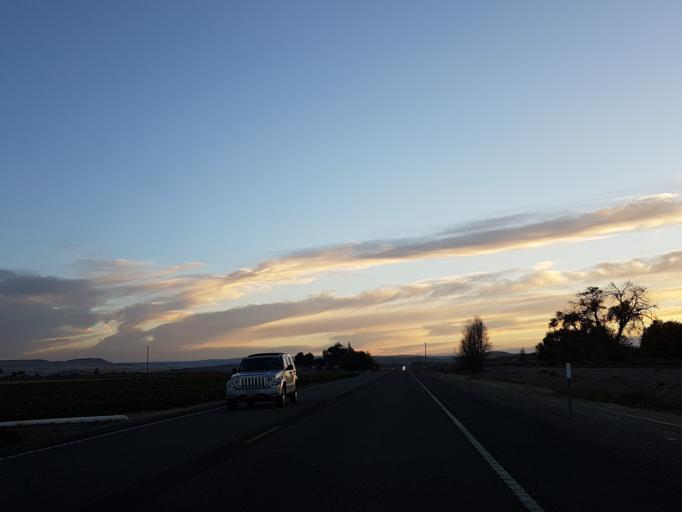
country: US
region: Oregon
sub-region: Malheur County
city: Vale
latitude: 43.9622
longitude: -117.2788
